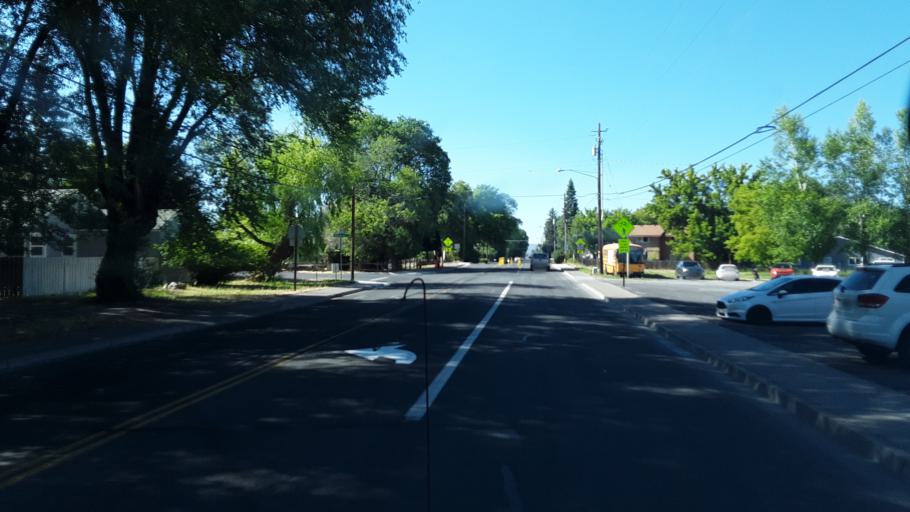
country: US
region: Oregon
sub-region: Klamath County
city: Altamont
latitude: 42.1991
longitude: -121.7228
